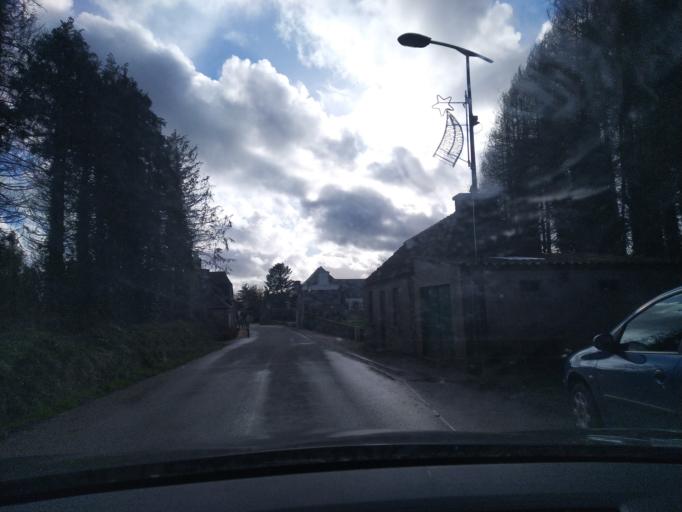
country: FR
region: Brittany
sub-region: Departement du Finistere
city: Guerlesquin
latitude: 48.4457
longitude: -3.5853
